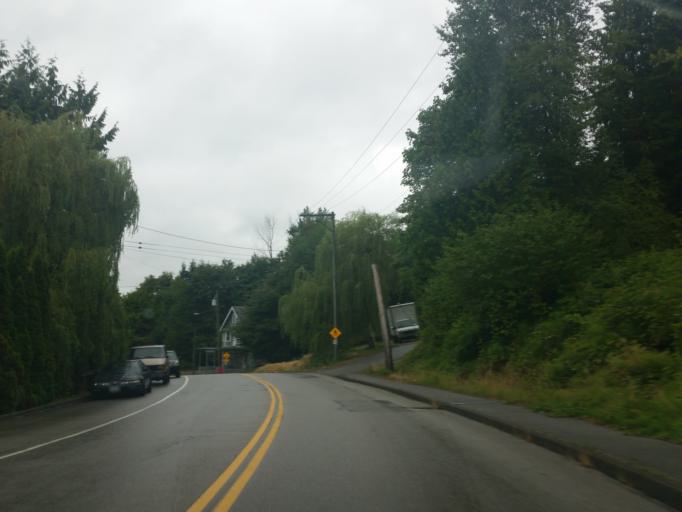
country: CA
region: British Columbia
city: Port Moody
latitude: 49.2907
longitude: -122.8434
